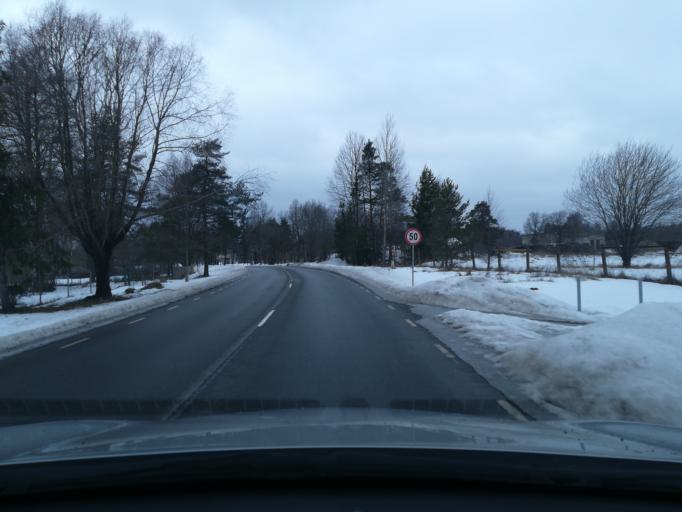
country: EE
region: Harju
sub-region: Nissi vald
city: Turba
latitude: 59.0718
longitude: 24.2487
